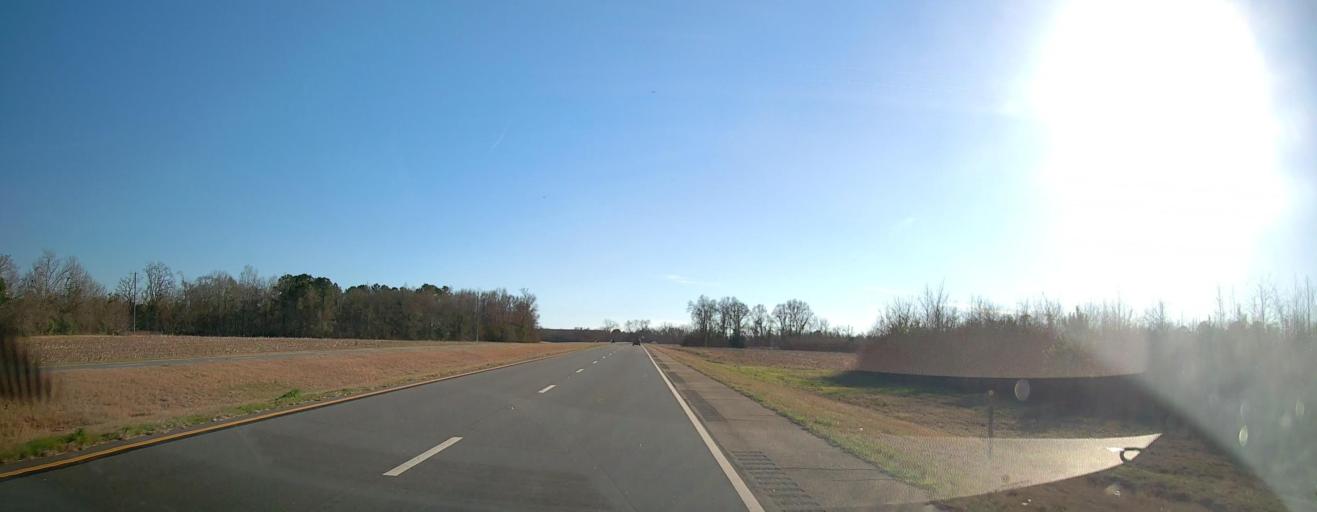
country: US
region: Georgia
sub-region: Sumter County
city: Americus
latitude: 31.9070
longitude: -84.2608
